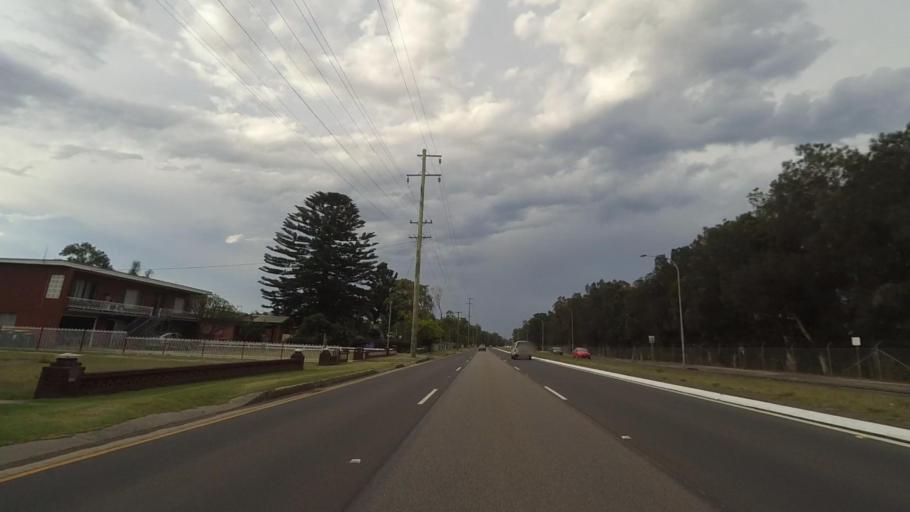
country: AU
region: New South Wales
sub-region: Wollongong
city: Lake Heights
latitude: -34.5161
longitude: 150.8726
